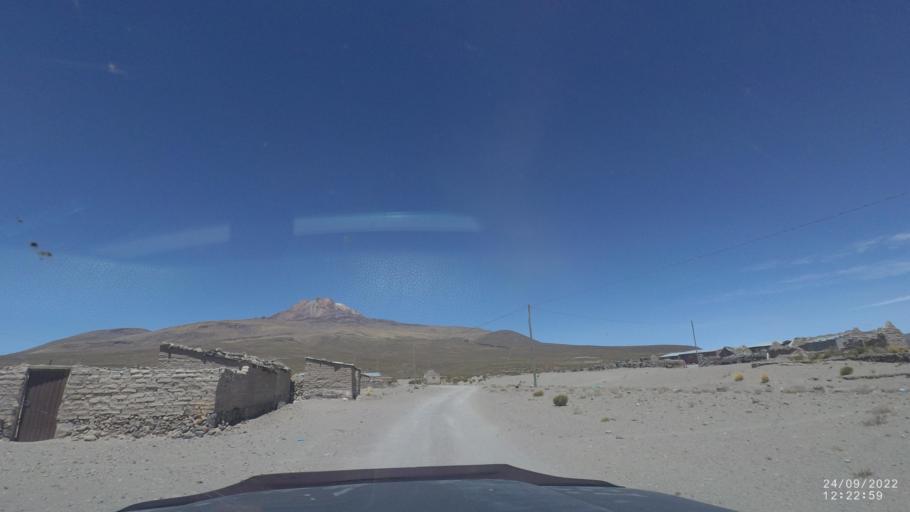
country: BO
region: Potosi
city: Colchani
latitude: -19.7606
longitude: -67.6644
